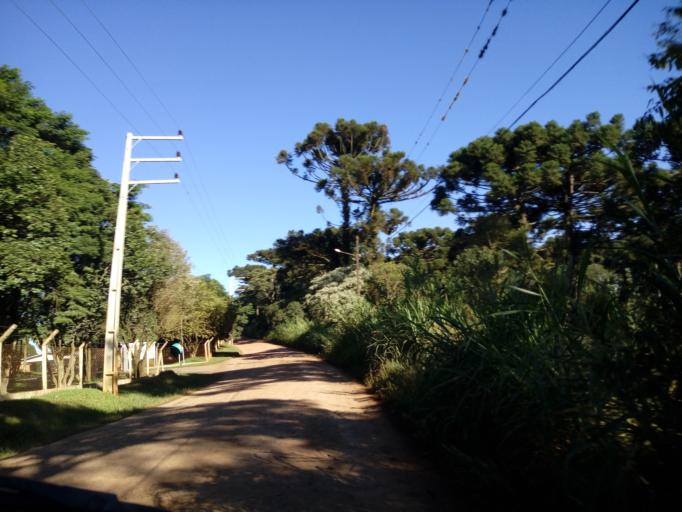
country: BR
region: Santa Catarina
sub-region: Chapeco
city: Chapeco
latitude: -27.1922
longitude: -52.6571
